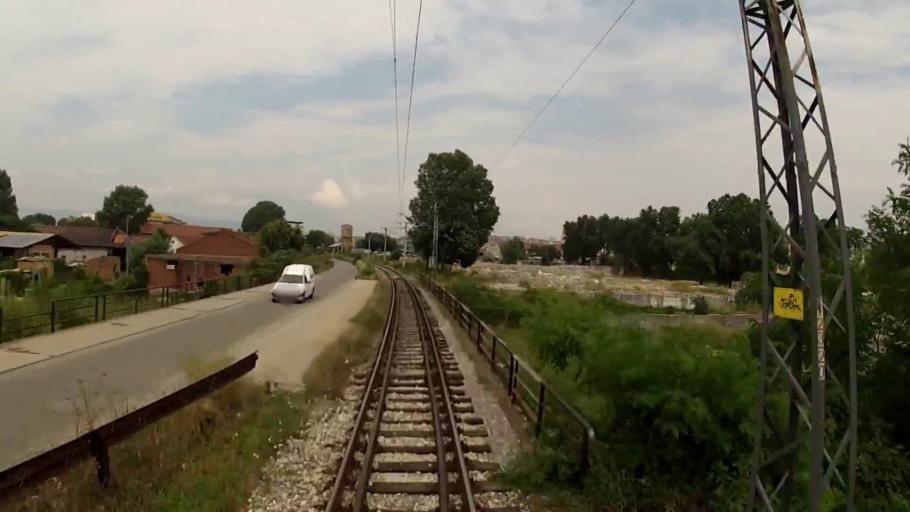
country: BG
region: Blagoevgrad
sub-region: Obshtina Blagoevgrad
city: Blagoevgrad
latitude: 41.9995
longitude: 23.0887
